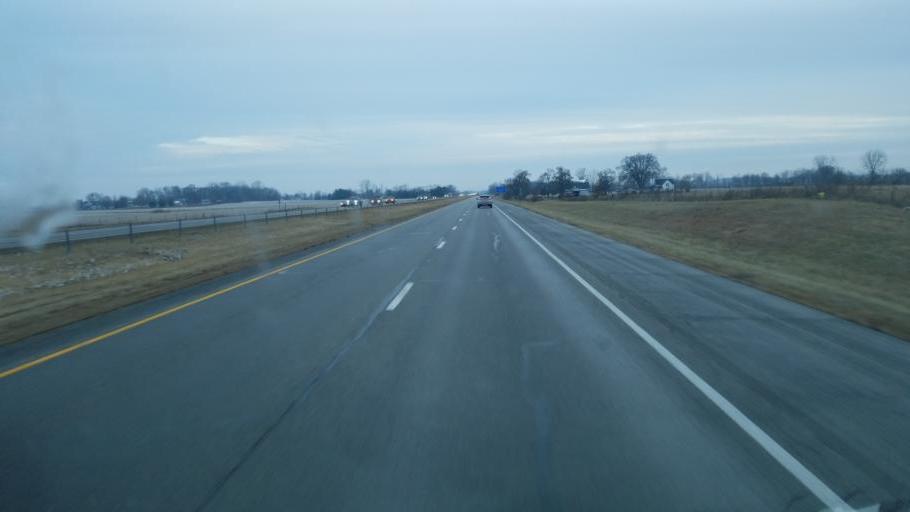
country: US
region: Indiana
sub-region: Hancock County
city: Greenfield
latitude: 39.8260
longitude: -85.6501
